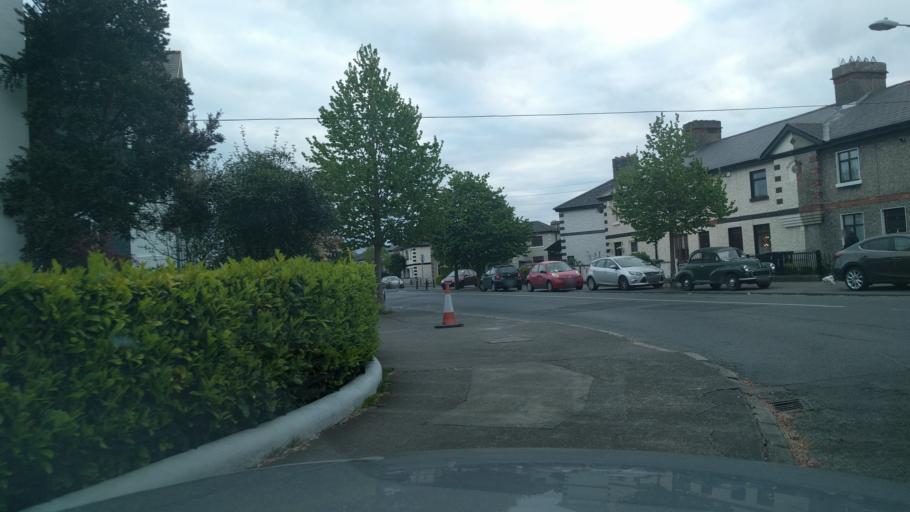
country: IE
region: Leinster
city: Rialto
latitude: 53.3367
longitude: -6.2794
